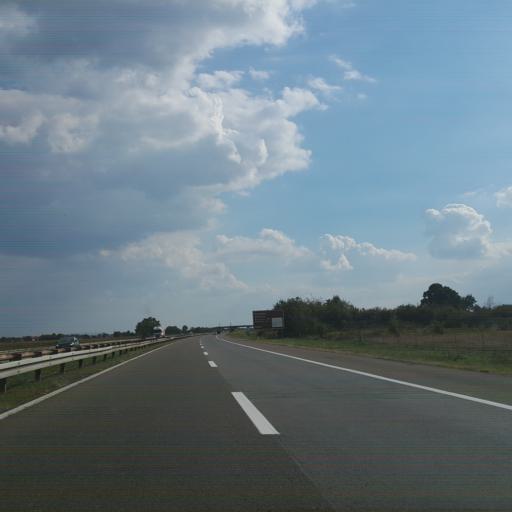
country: RS
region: Central Serbia
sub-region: Podunavski Okrug
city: Velika Plana
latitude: 44.3294
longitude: 21.0891
